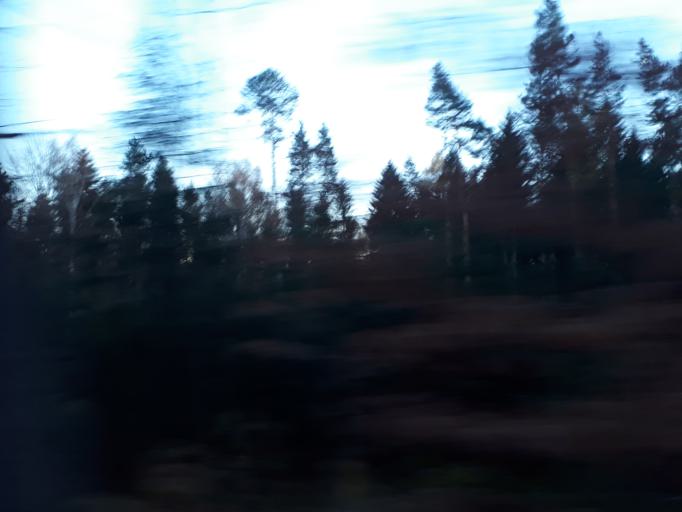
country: DE
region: Saxony
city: Reinhardtsgrimma
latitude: 50.8964
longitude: 13.7769
